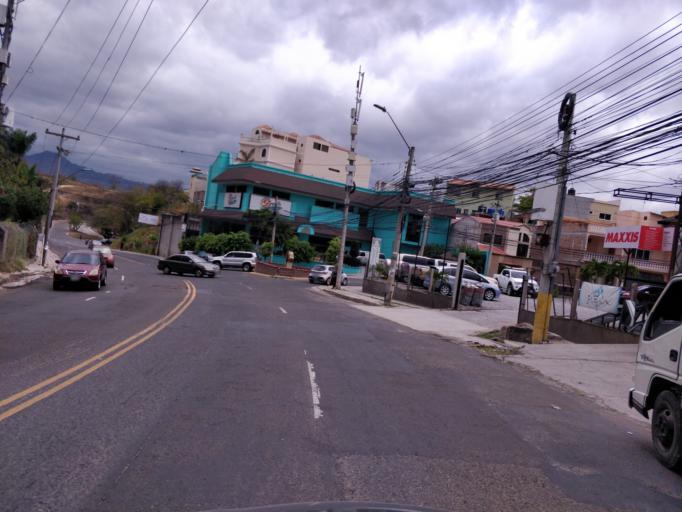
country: HN
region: Francisco Morazan
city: Tegucigalpa
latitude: 14.0501
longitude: -87.2158
